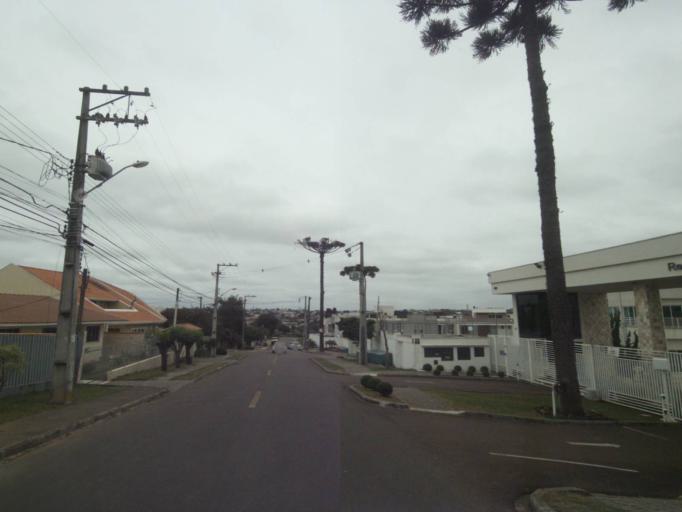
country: BR
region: Parana
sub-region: Sao Jose Dos Pinhais
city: Sao Jose dos Pinhais
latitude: -25.4818
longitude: -49.2353
